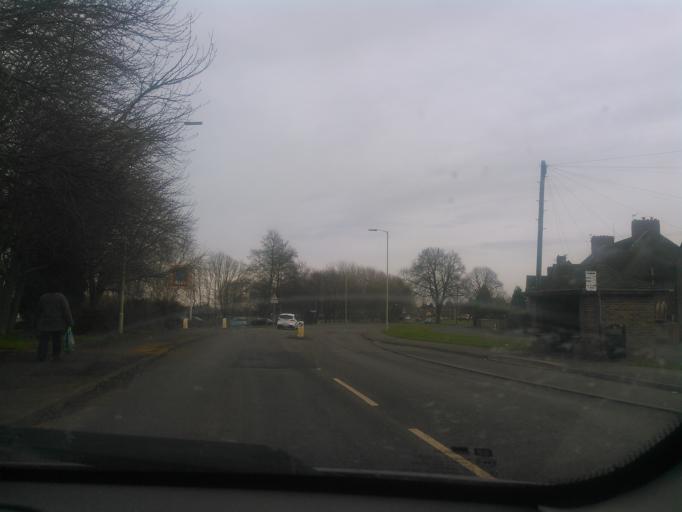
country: GB
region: England
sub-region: Telford and Wrekin
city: Oakengates
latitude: 52.7200
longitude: -2.4409
